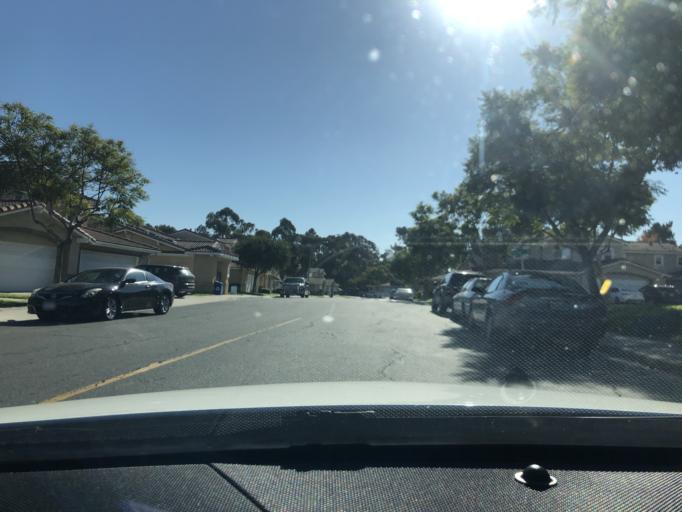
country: US
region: California
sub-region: San Diego County
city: Lemon Grove
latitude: 32.7401
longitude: -117.0622
